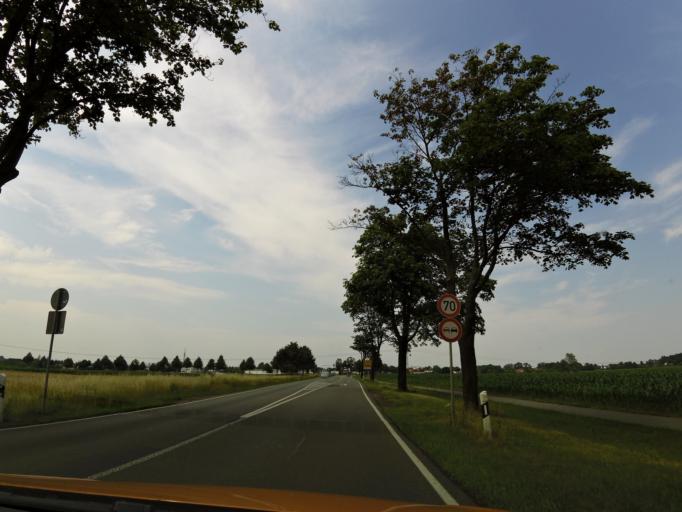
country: DE
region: Brandenburg
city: Kyritz
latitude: 52.9318
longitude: 12.4134
